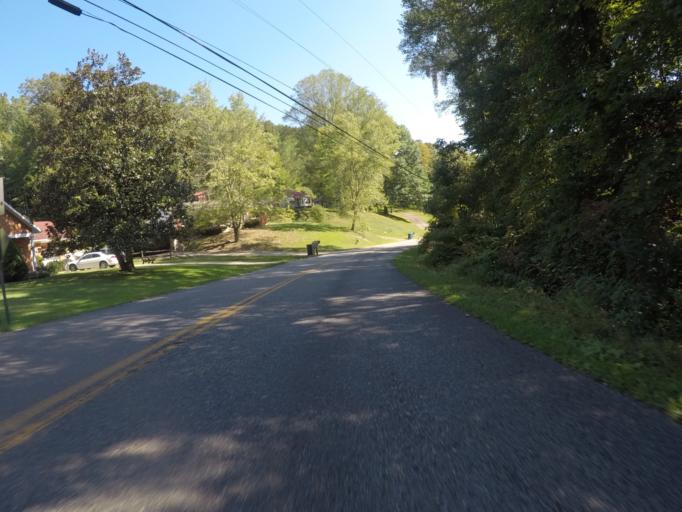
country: US
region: Kentucky
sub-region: Greenup County
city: Russell
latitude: 38.5235
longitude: -82.6941
